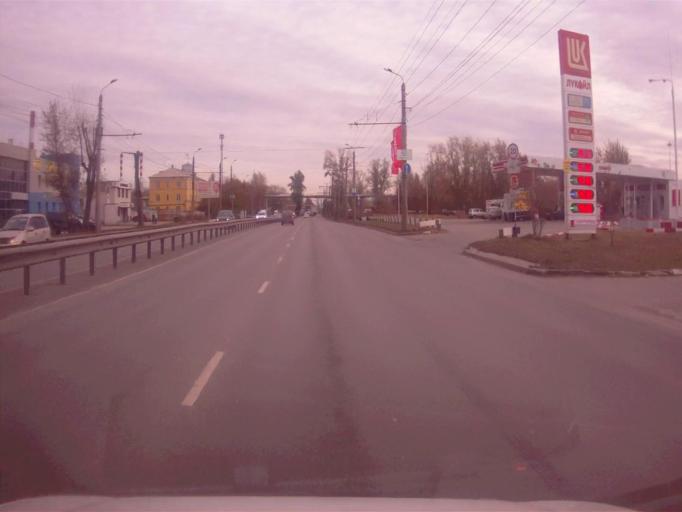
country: RU
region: Chelyabinsk
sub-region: Gorod Chelyabinsk
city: Chelyabinsk
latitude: 55.1357
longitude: 61.4640
